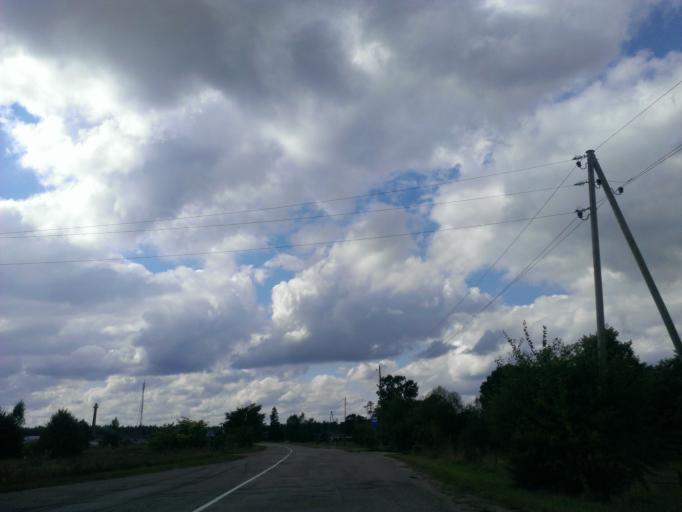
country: LV
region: Ropazu
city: Ropazi
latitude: 56.9657
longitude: 24.5145
